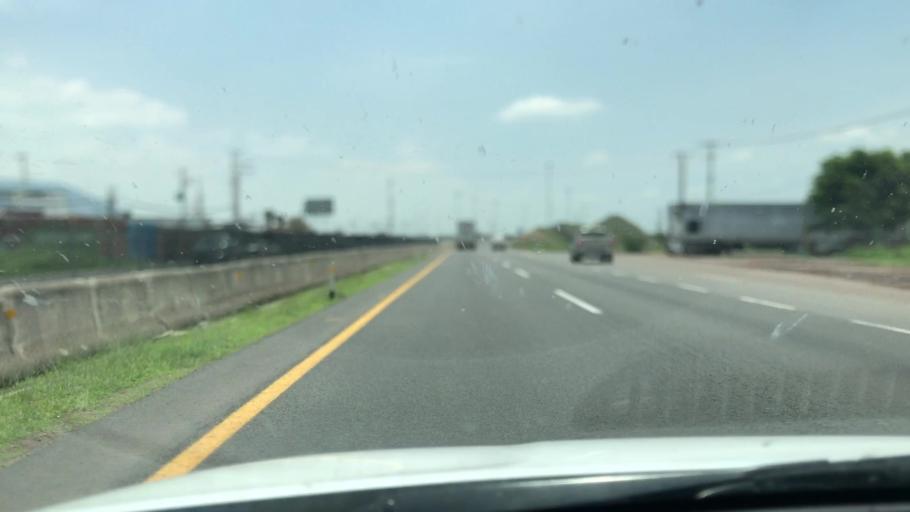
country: MX
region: Guanajuato
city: Penjamo
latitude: 20.4173
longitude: -101.7272
